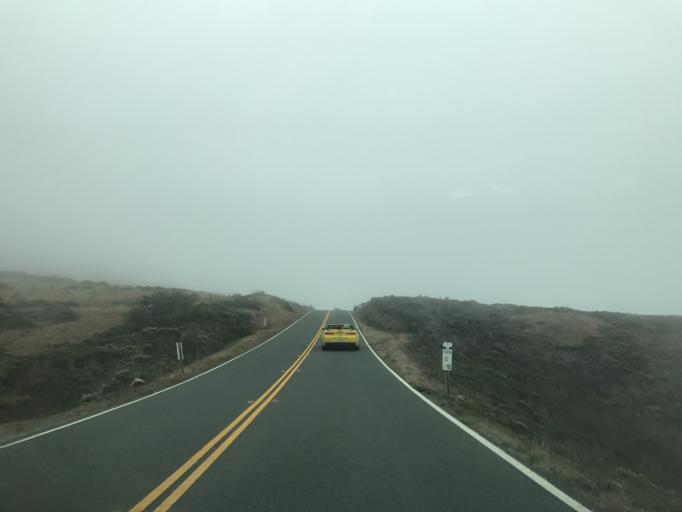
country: US
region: California
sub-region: Sonoma County
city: Monte Rio
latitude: 38.4642
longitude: -123.1504
